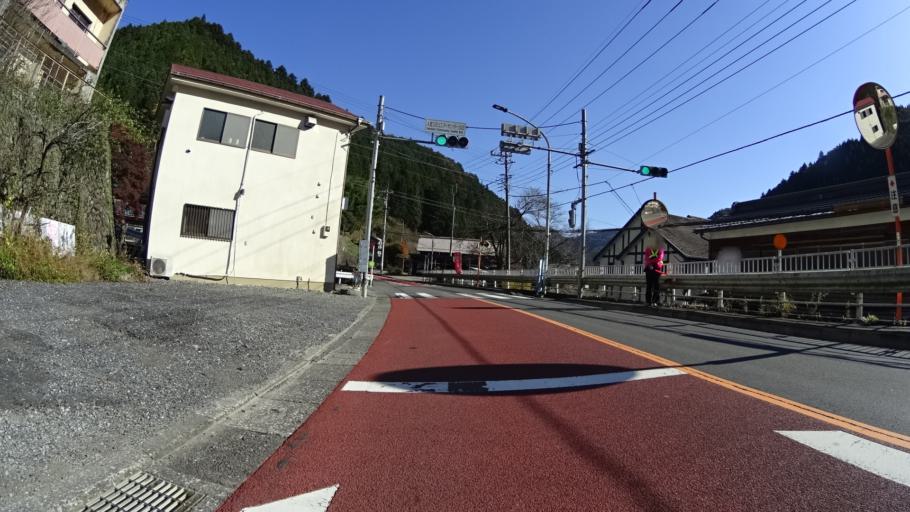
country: JP
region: Yamanashi
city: Uenohara
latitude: 35.7130
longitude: 139.0890
